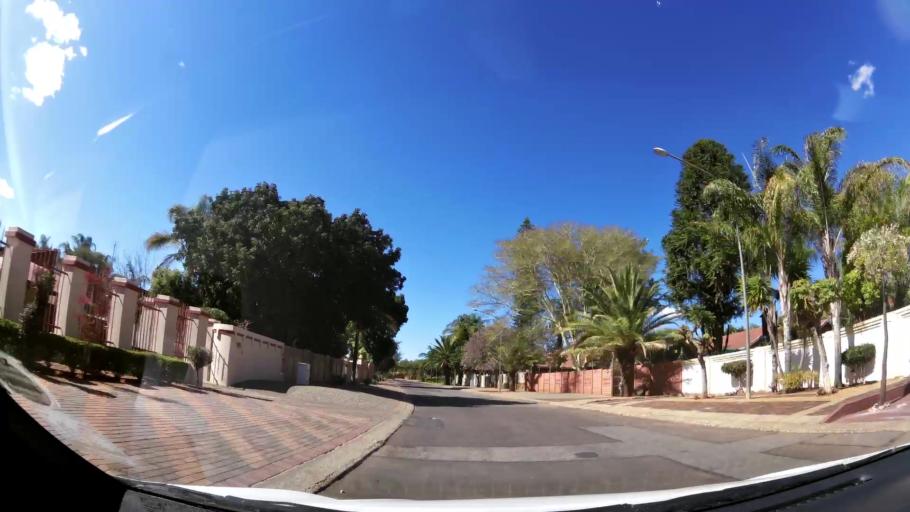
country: ZA
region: Limpopo
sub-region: Capricorn District Municipality
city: Polokwane
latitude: -23.9169
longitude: 29.4844
